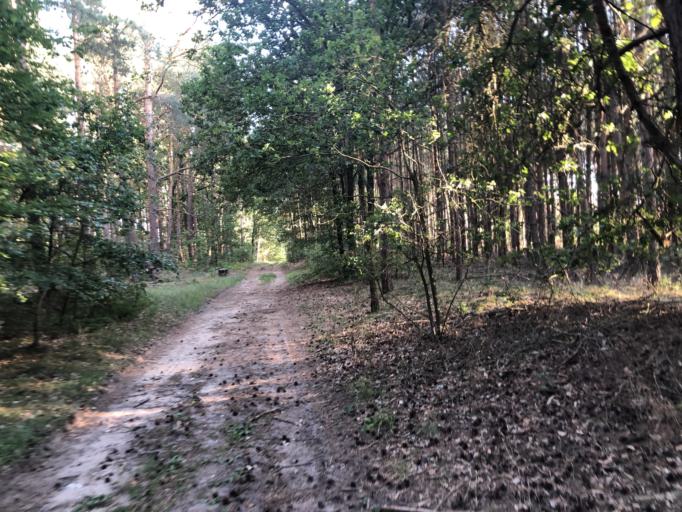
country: DE
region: Lower Saxony
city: Tosterglope
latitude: 53.2568
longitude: 10.7908
